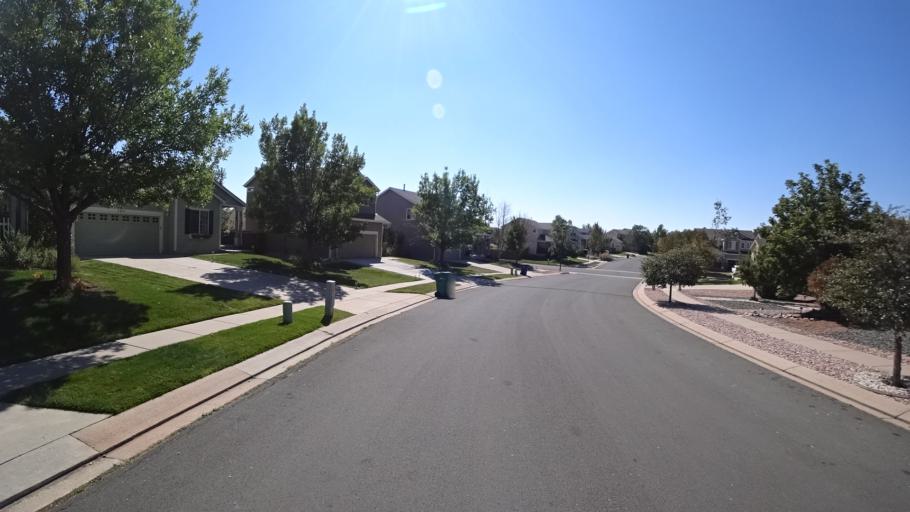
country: US
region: Colorado
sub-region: El Paso County
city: Cimarron Hills
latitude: 38.8848
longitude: -104.6930
